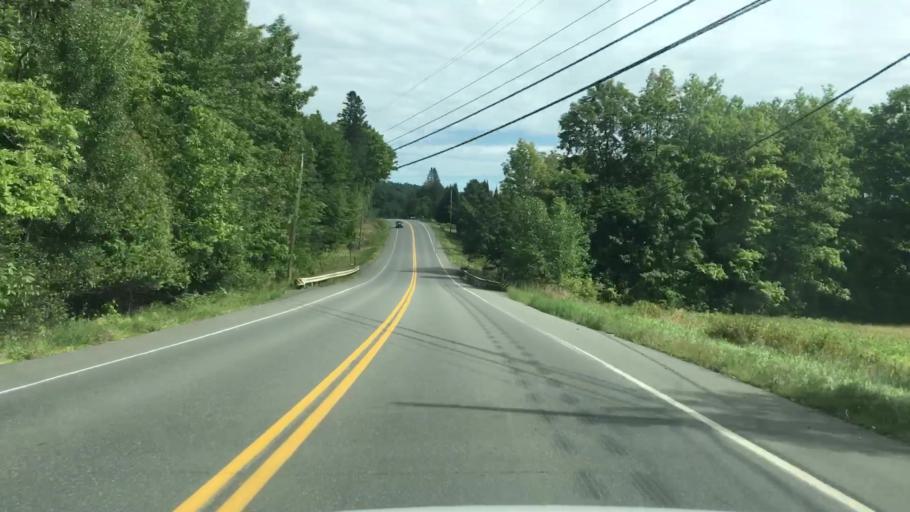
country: US
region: Maine
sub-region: Piscataquis County
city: Dover-Foxcroft
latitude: 45.2025
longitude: -69.1876
